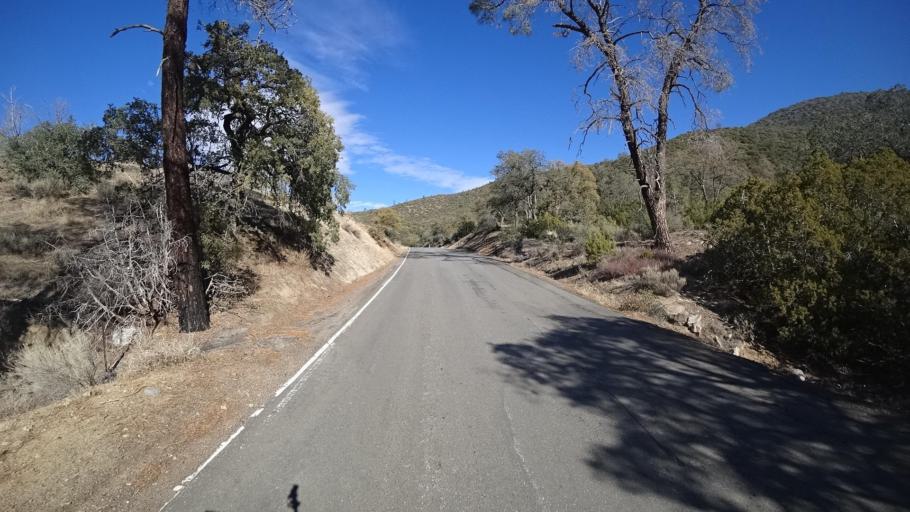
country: US
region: California
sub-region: Kern County
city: Bodfish
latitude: 35.5617
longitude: -118.5051
